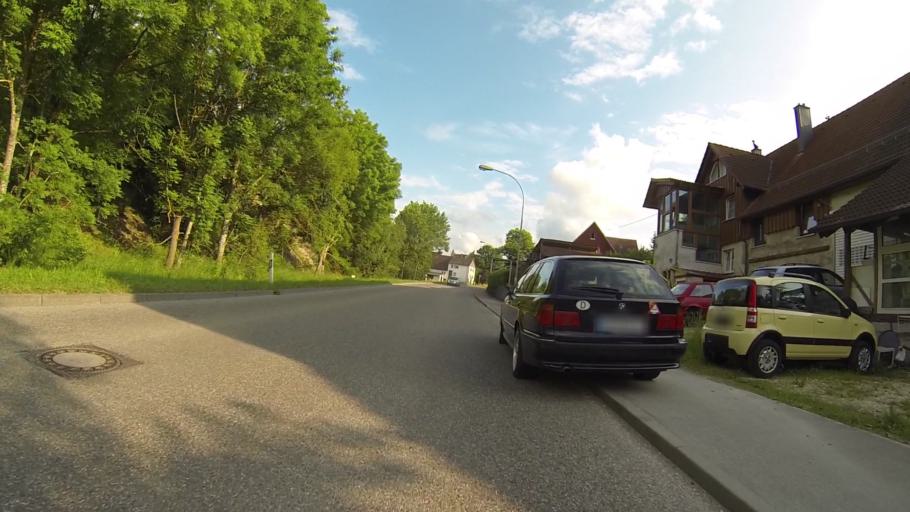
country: DE
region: Baden-Wuerttemberg
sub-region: Regierungsbezirk Stuttgart
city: Nattheim
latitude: 48.7361
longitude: 10.2647
